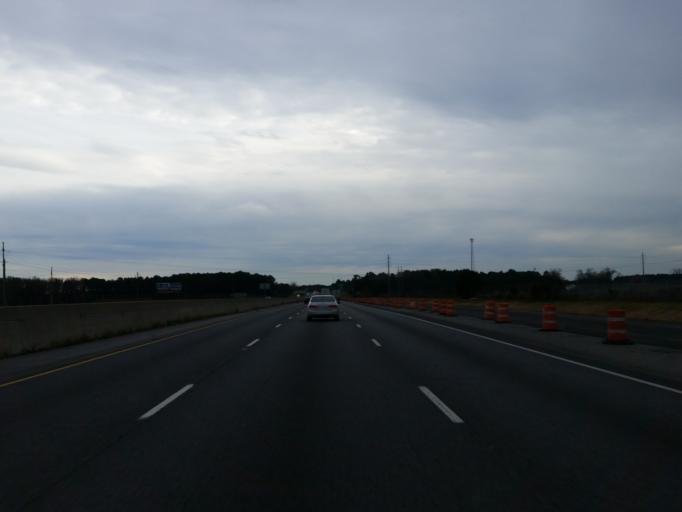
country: US
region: Georgia
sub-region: Tift County
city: Tifton
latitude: 31.5006
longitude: -83.5155
